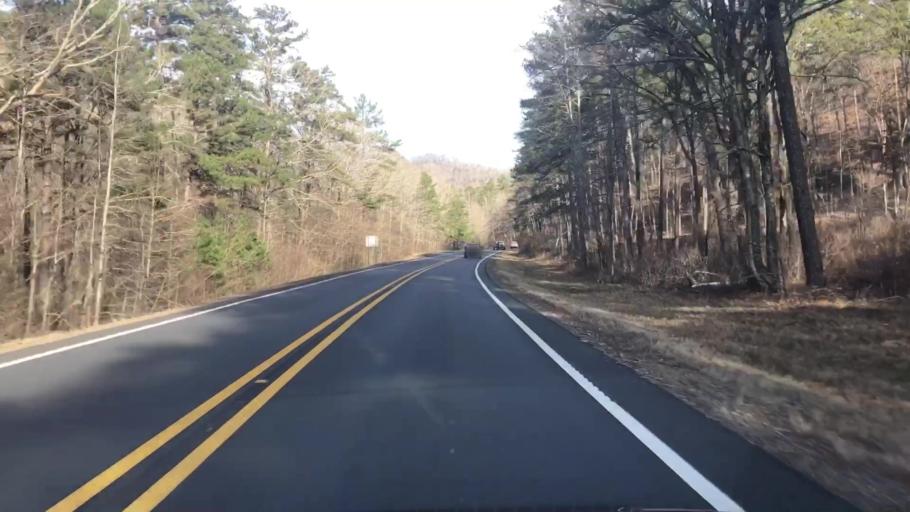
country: US
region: Arkansas
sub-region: Montgomery County
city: Mount Ida
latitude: 34.5201
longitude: -93.3892
